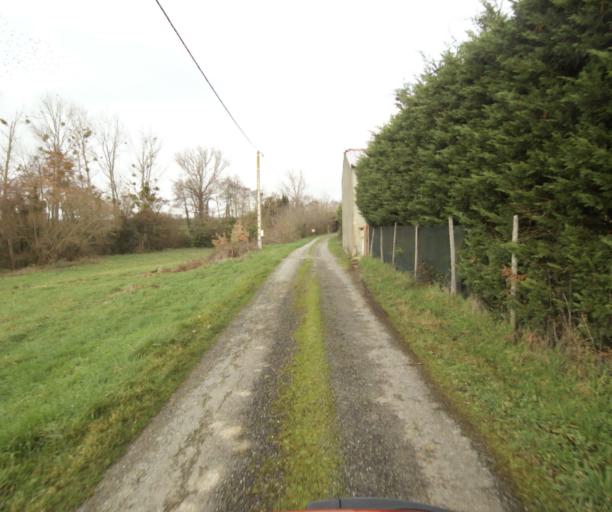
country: FR
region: Languedoc-Roussillon
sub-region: Departement de l'Aude
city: Belpech
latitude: 43.1612
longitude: 1.6949
